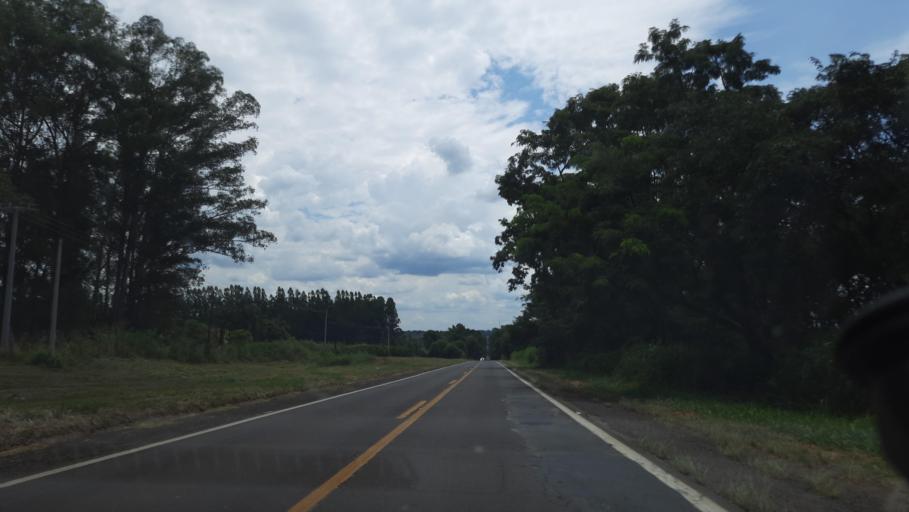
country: BR
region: Sao Paulo
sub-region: Mococa
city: Mococa
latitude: -21.5052
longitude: -47.0523
